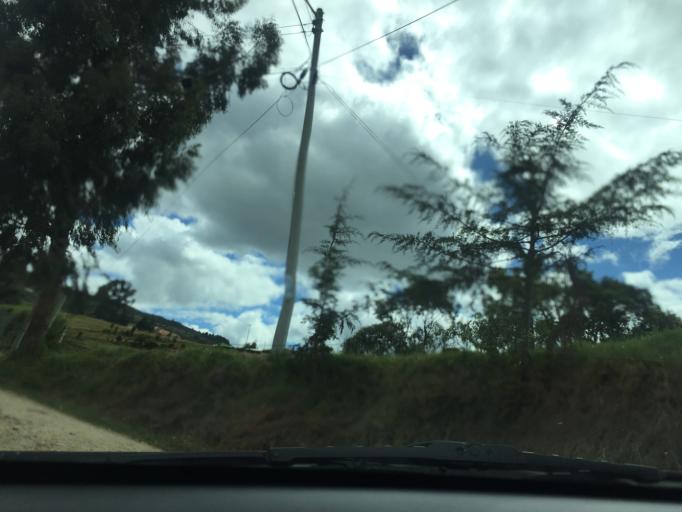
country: CO
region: Cundinamarca
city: Tocancipa
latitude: 4.9634
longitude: -73.8976
